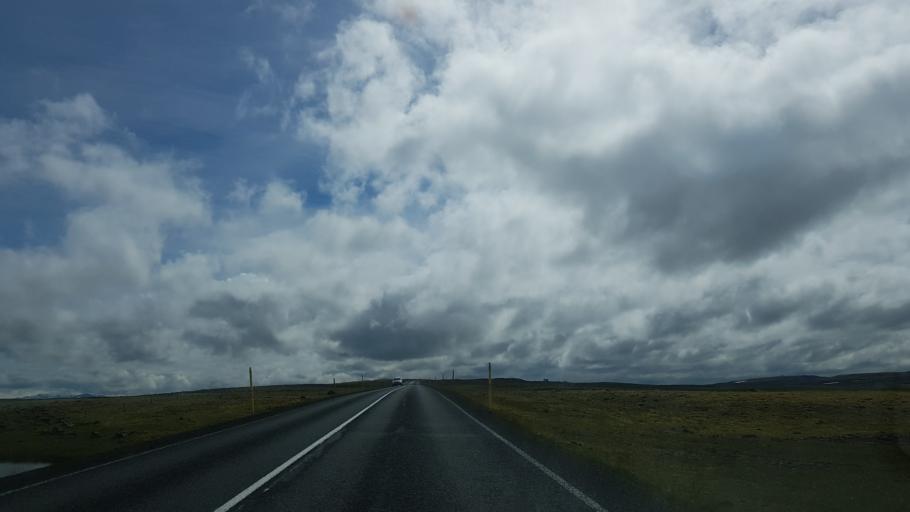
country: IS
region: West
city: Borgarnes
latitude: 65.0094
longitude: -21.0672
